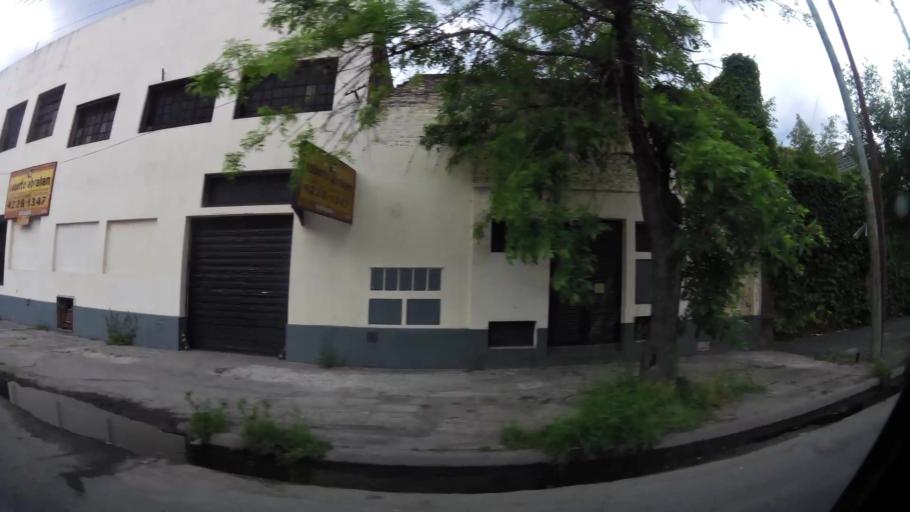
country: AR
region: Buenos Aires
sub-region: Partido de Lanus
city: Lanus
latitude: -34.6885
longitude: -58.3900
